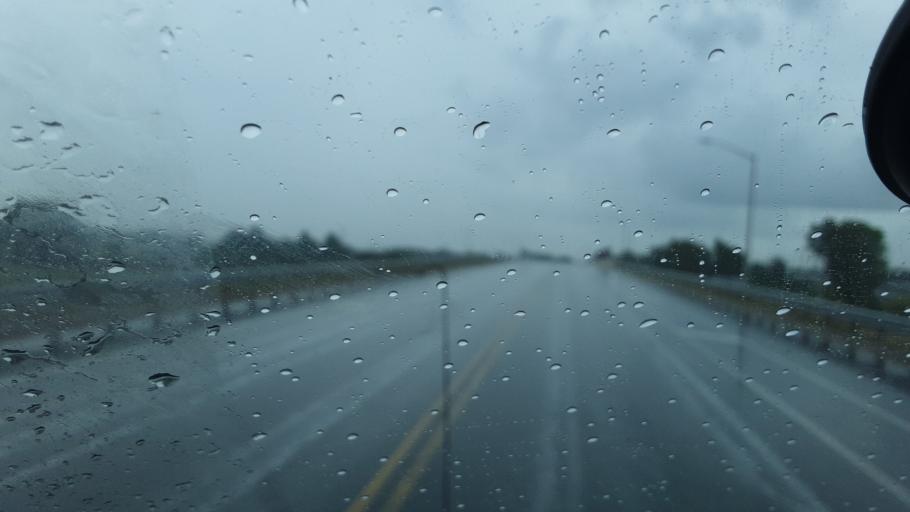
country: US
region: Ohio
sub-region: Williams County
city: Montpelier
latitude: 41.5869
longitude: -84.5812
